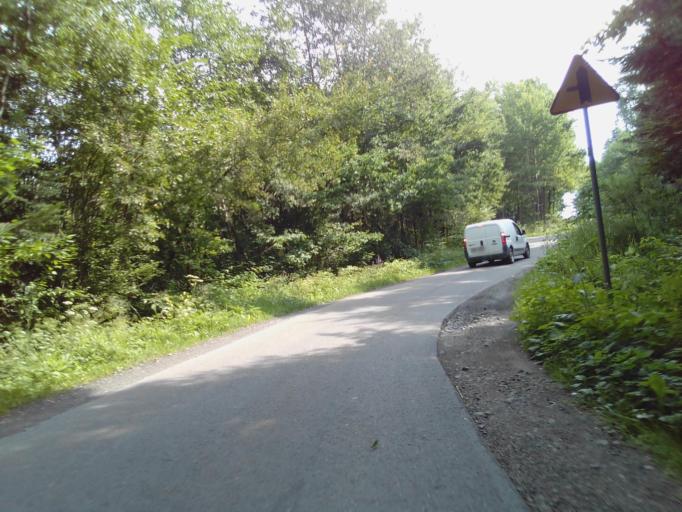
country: PL
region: Subcarpathian Voivodeship
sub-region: Powiat strzyzowski
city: Frysztak
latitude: 49.8603
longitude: 21.5373
